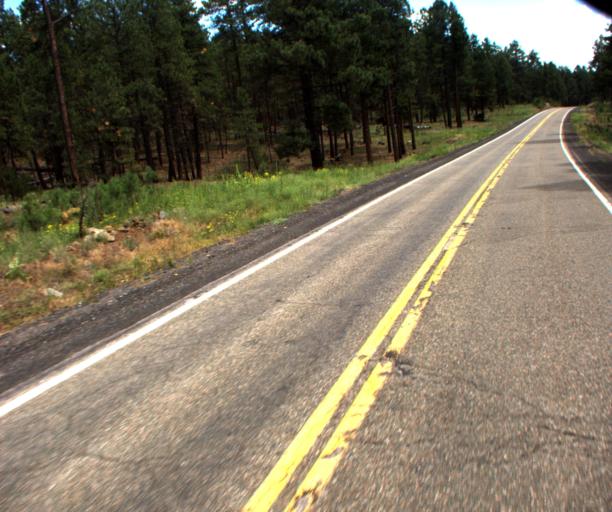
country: US
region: Arizona
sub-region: Coconino County
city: Flagstaff
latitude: 35.3050
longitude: -111.7697
